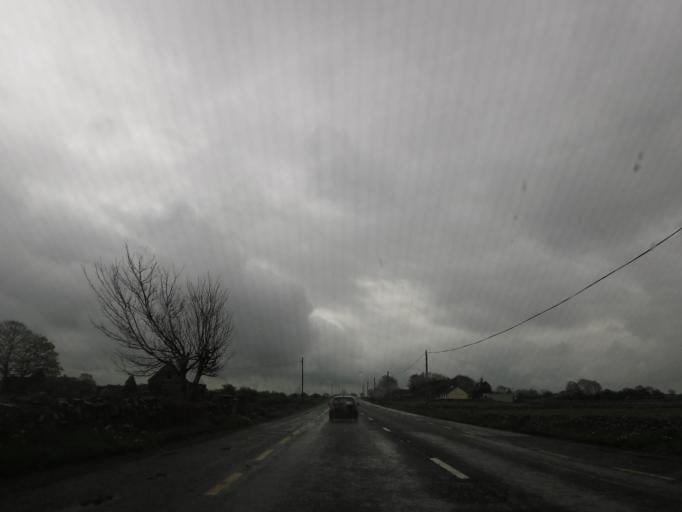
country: IE
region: Connaught
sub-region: County Galway
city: Claregalway
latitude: 53.4020
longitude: -8.9116
